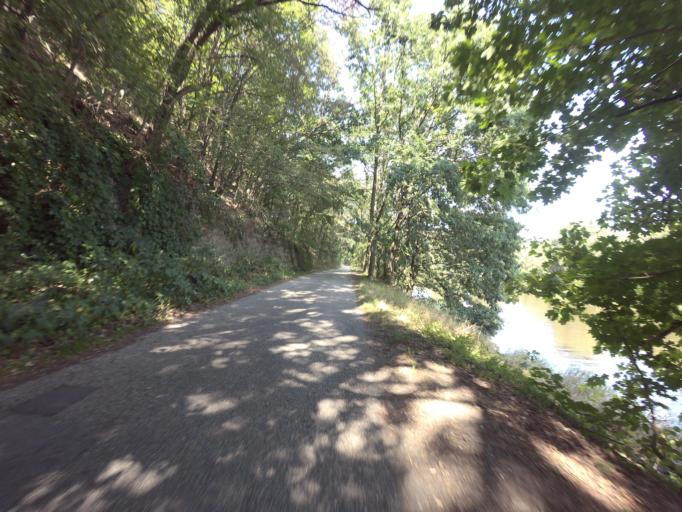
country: CZ
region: Jihocesky
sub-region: Okres Ceske Budejovice
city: Hluboka nad Vltavou
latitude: 49.0586
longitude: 14.4421
